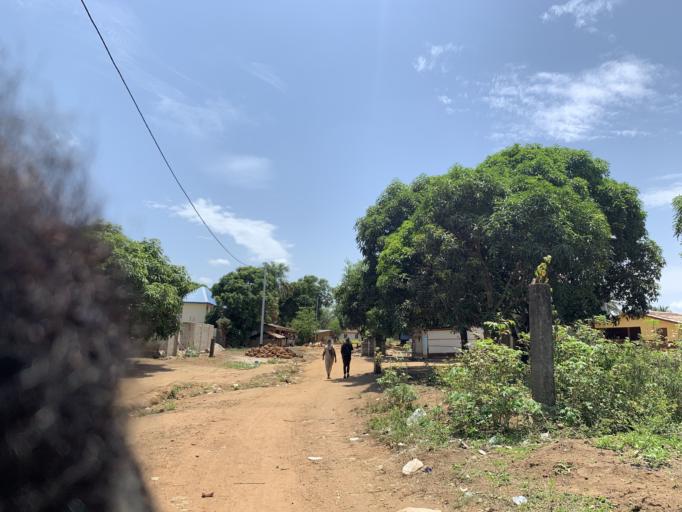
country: SL
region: Western Area
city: Waterloo
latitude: 8.3107
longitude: -13.0721
